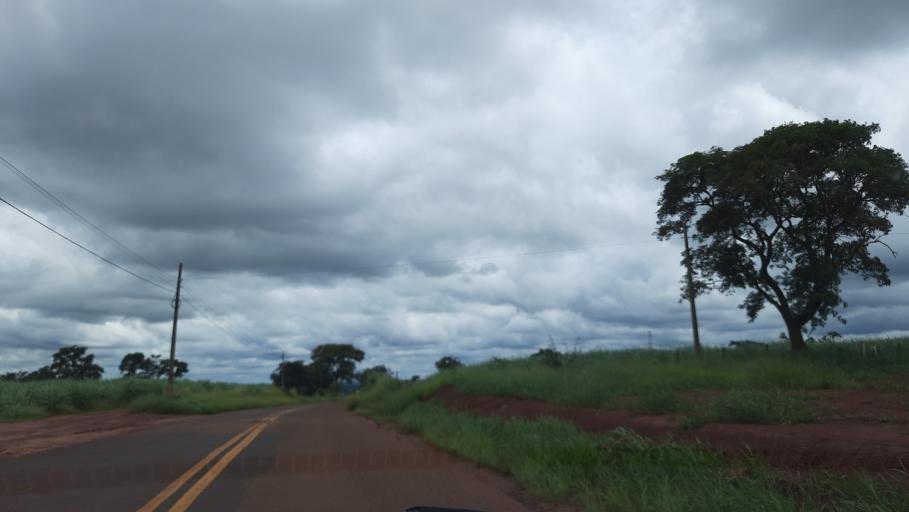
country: BR
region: Sao Paulo
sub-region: Casa Branca
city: Casa Branca
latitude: -21.7972
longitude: -47.0967
